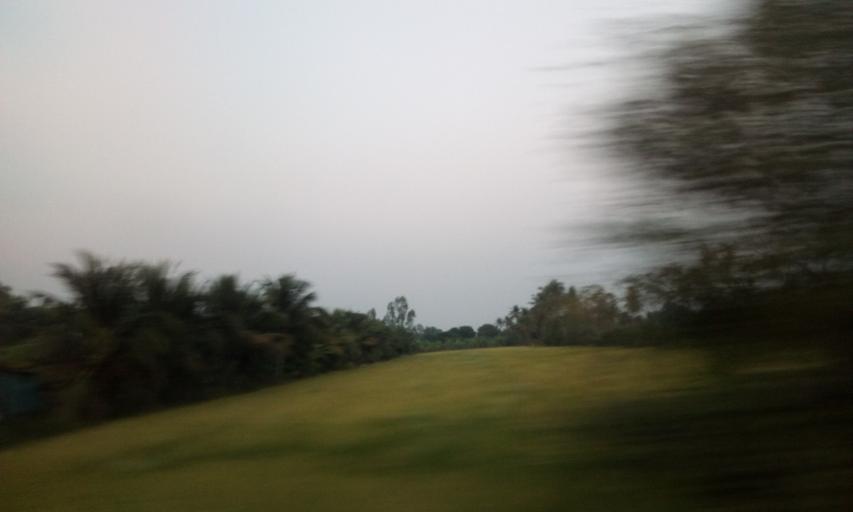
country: TH
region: Sing Buri
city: Sing Buri
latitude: 14.8327
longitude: 100.4003
